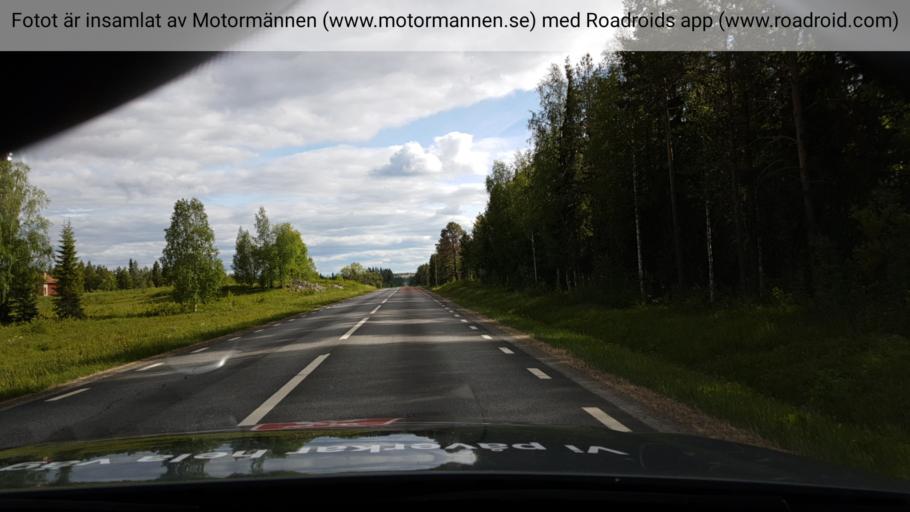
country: SE
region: Jaemtland
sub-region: Stroemsunds Kommun
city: Stroemsund
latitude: 63.7734
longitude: 15.5057
